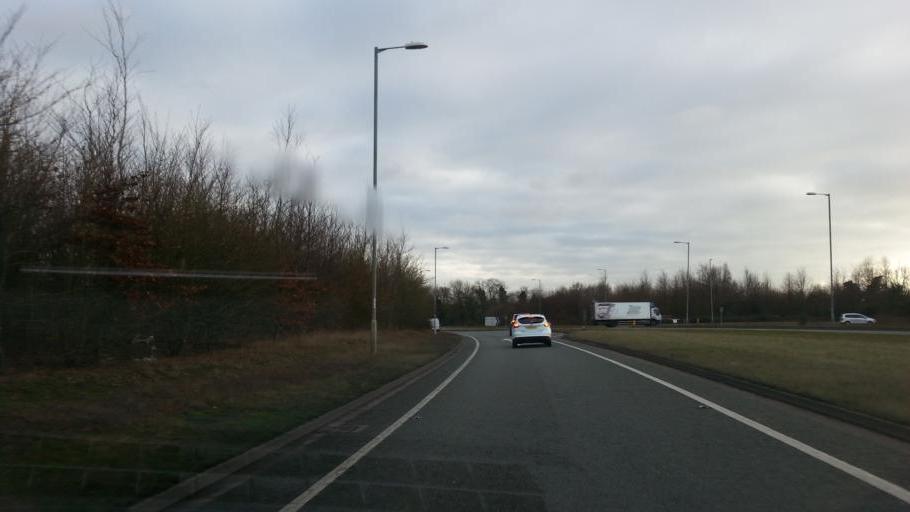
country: GB
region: England
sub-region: Cambridgeshire
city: Fulbourn
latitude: 52.1273
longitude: 0.2256
